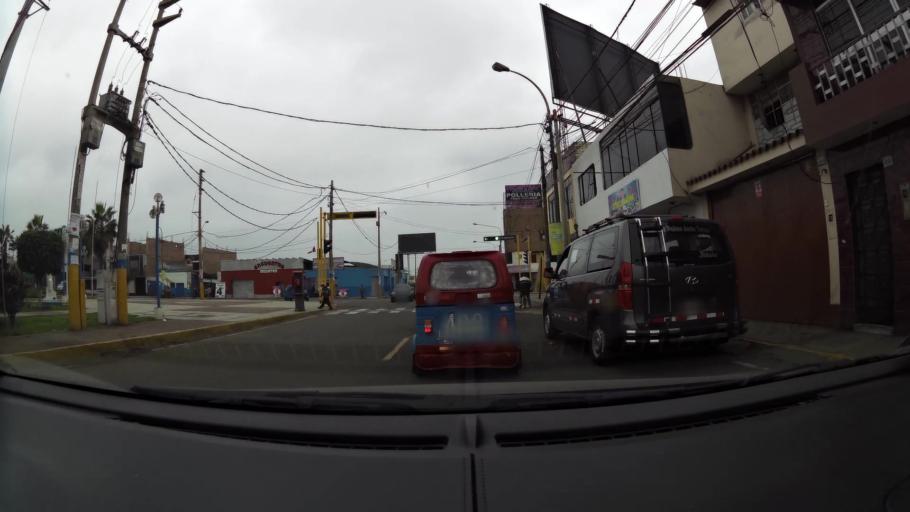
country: PE
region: Lima
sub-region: Barranca
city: Barranca
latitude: -10.7565
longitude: -77.7565
